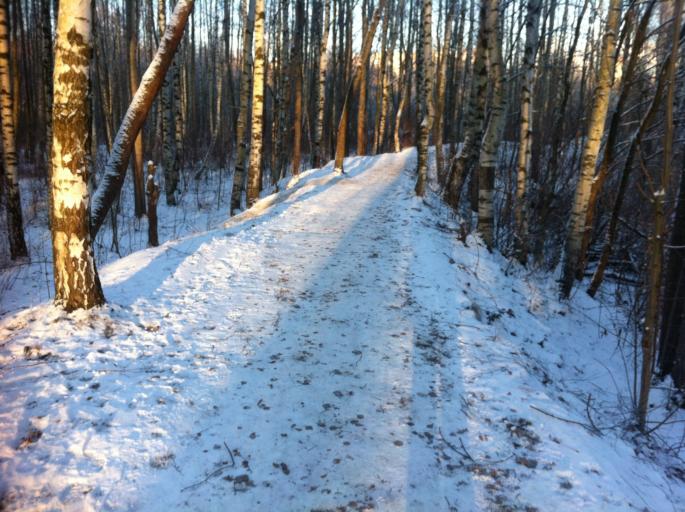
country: RU
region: St.-Petersburg
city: Uritsk
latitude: 59.8532
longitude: 30.1626
